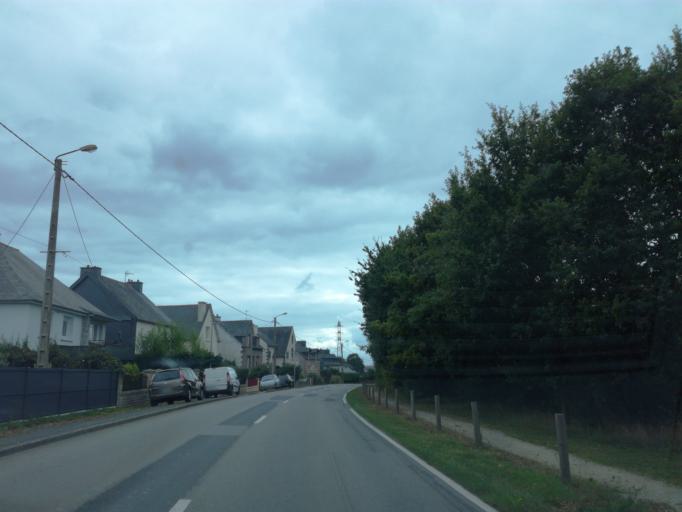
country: FR
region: Brittany
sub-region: Departement des Cotes-d'Armor
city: Loudeac
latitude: 48.1694
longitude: -2.7536
